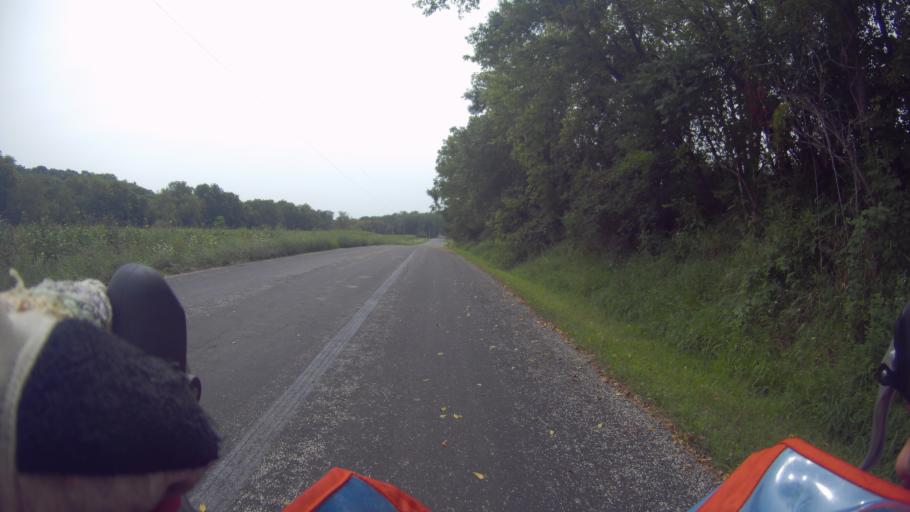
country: US
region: Wisconsin
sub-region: Dane County
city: Mount Horeb
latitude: 42.9798
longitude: -89.6763
